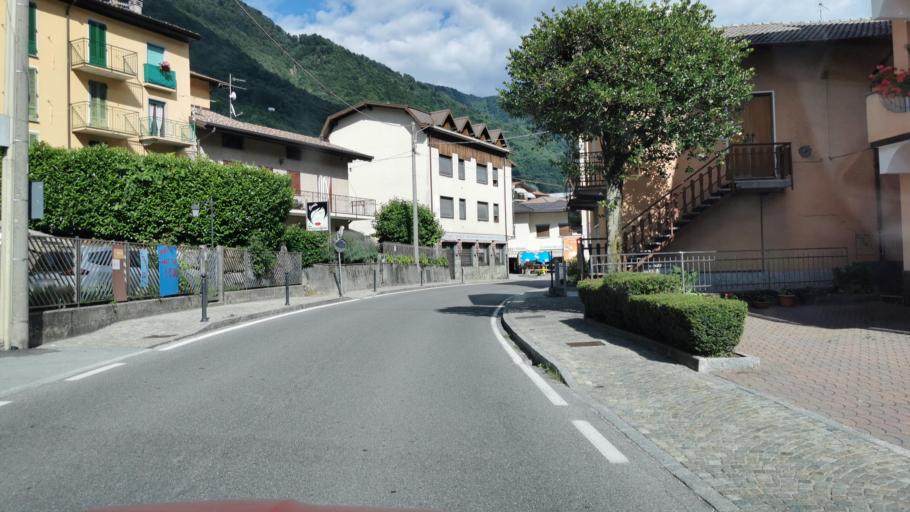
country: IT
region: Lombardy
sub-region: Provincia di Lecco
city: Primaluna
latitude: 45.9862
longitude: 9.4308
